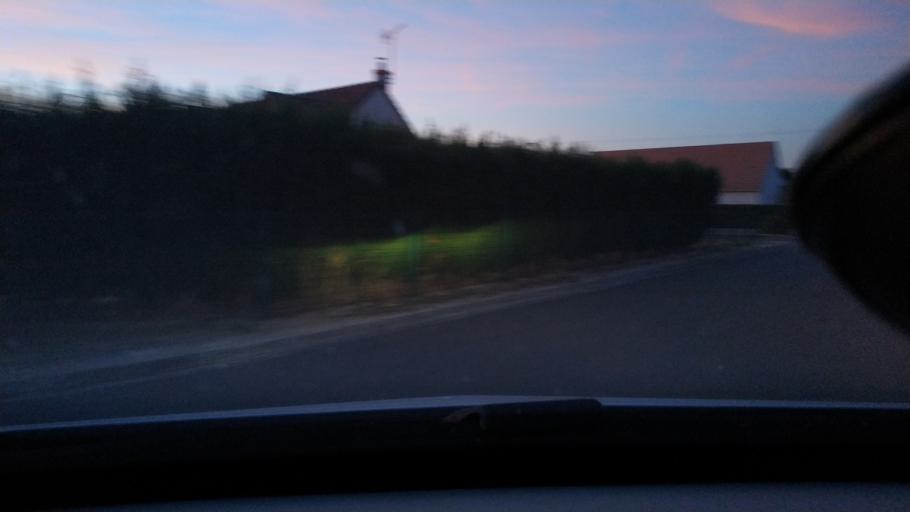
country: FR
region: Centre
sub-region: Departement du Cher
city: Brinon-sur-Sauldre
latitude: 47.6102
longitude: 2.1679
